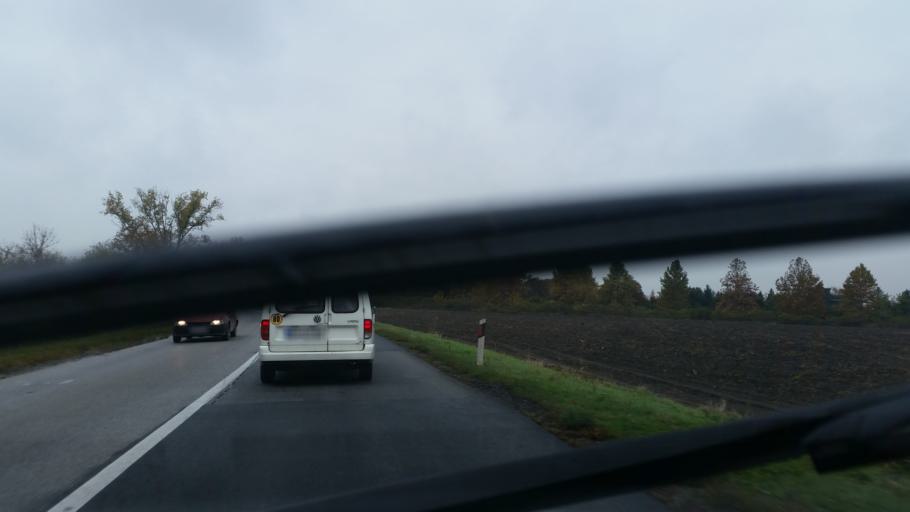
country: RS
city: Sefkerin
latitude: 44.9520
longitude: 20.4312
